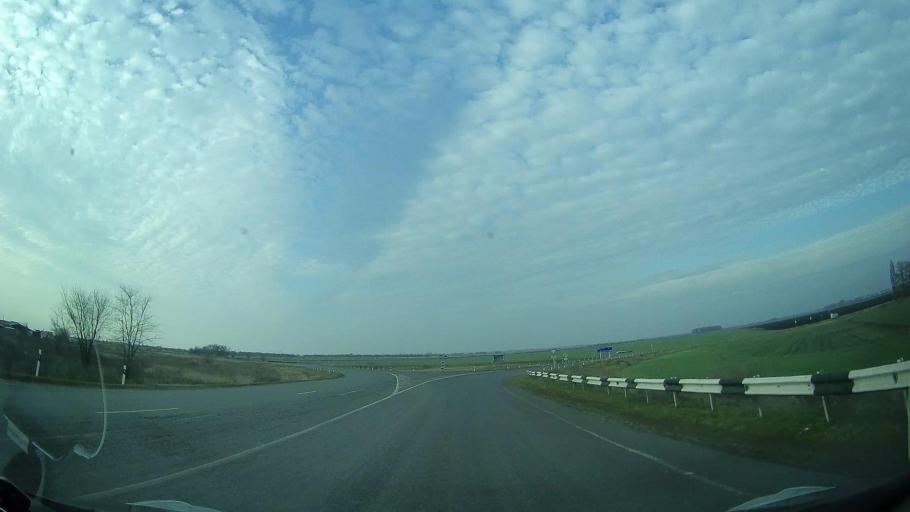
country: RU
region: Rostov
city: Bagayevskaya
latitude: 47.1650
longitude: 40.2726
